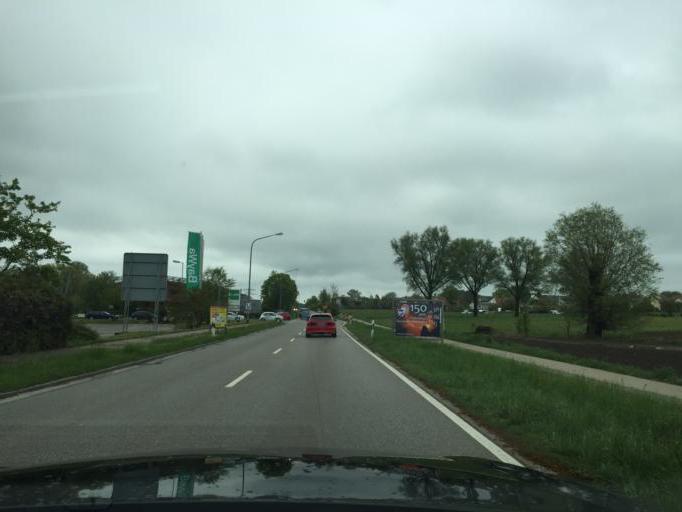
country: DE
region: Bavaria
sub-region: Swabia
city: Wertingen
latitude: 48.5581
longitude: 10.6928
